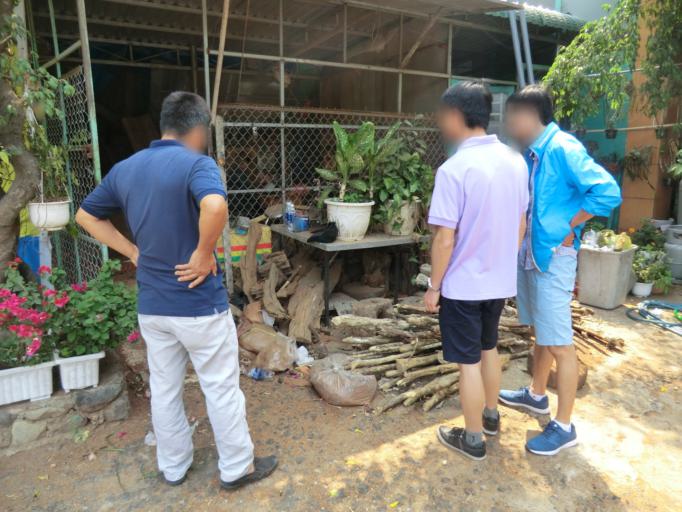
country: VN
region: Lam Dong
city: Ma Da Gui
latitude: 11.4250
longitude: 107.6877
